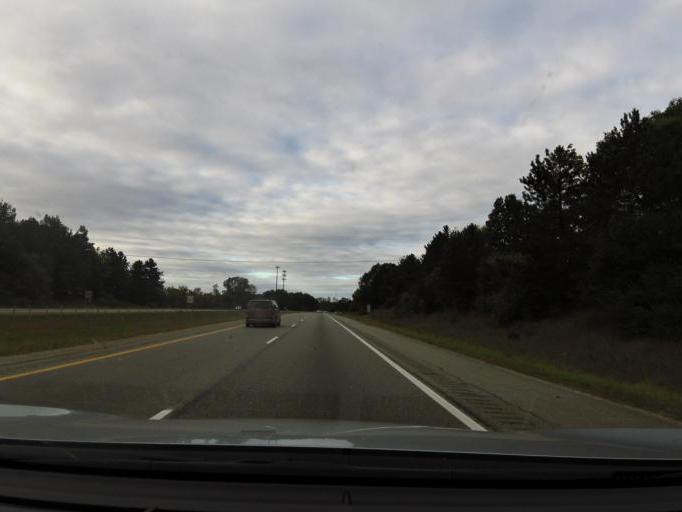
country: US
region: Michigan
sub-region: Livingston County
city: Brighton
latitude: 42.5443
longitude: -83.7490
